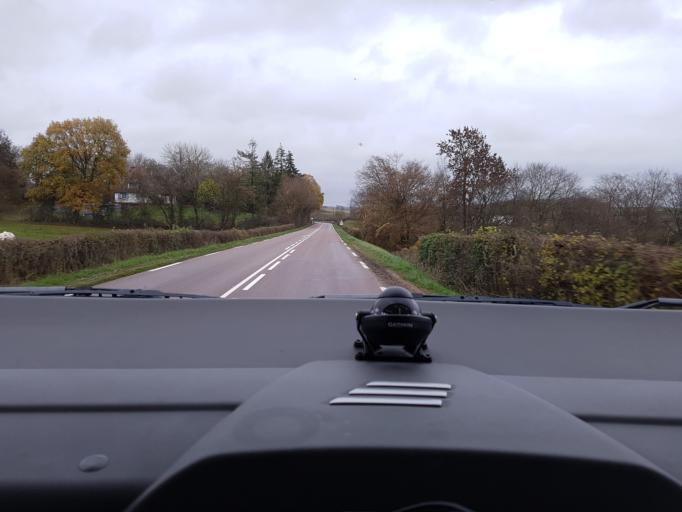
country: FR
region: Picardie
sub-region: Departement de l'Oise
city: Songeons
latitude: 49.5257
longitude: 1.8426
